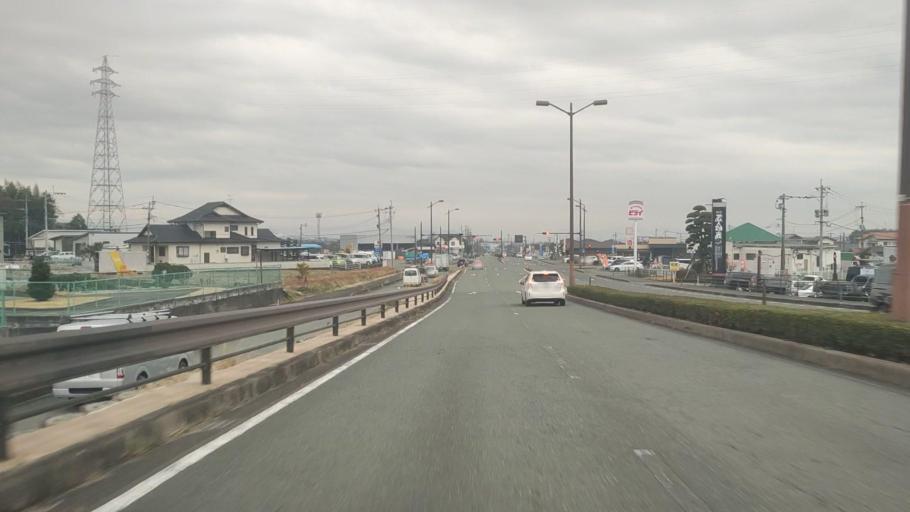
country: JP
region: Kumamoto
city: Ozu
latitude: 32.8347
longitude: 130.8013
